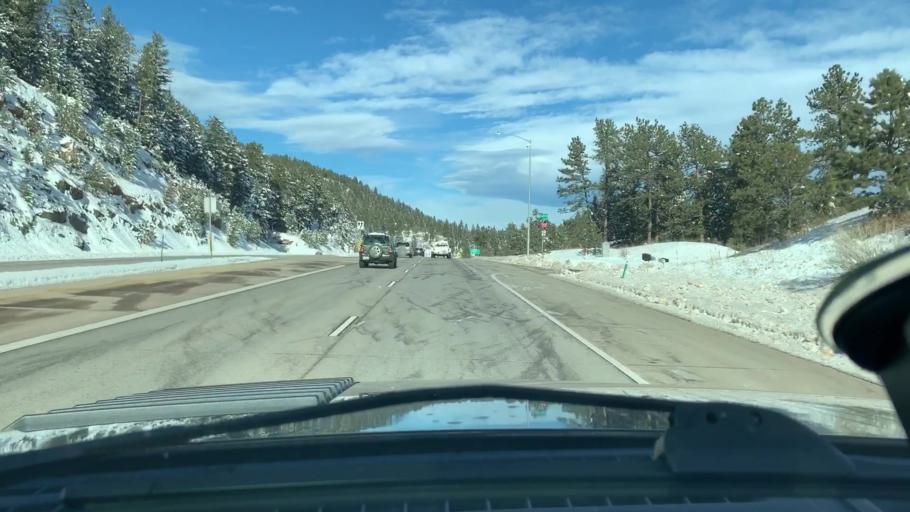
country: US
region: Colorado
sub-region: Jefferson County
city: Indian Hills
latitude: 39.5984
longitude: -105.2259
